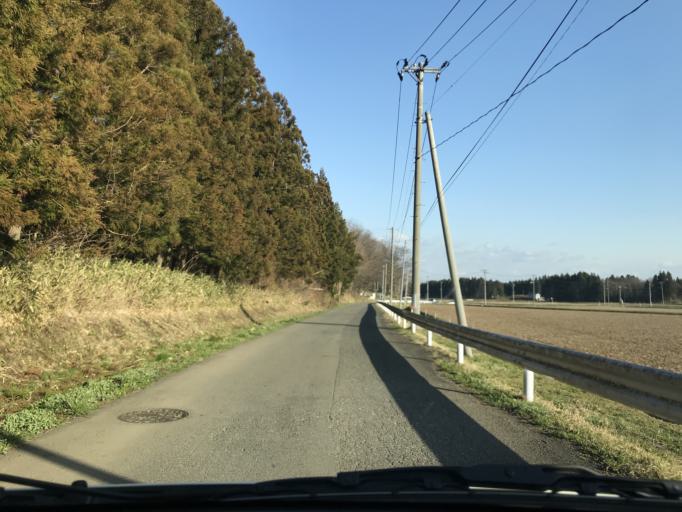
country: JP
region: Iwate
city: Kitakami
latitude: 39.2394
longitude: 141.0729
